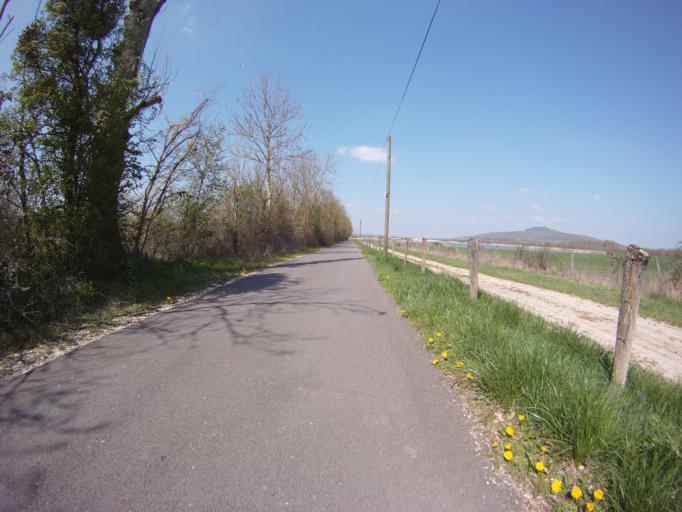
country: FR
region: Lorraine
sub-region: Departement de Meurthe-et-Moselle
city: Blenod-les-Pont-a-Mousson
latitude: 48.8746
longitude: 6.0677
